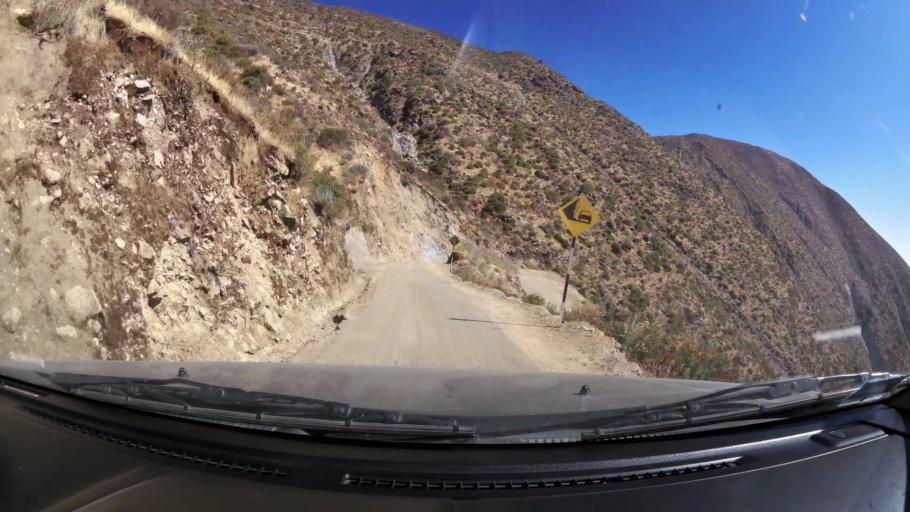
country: PE
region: Huancavelica
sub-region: Huaytara
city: Quito-Arma
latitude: -13.6203
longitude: -75.3531
